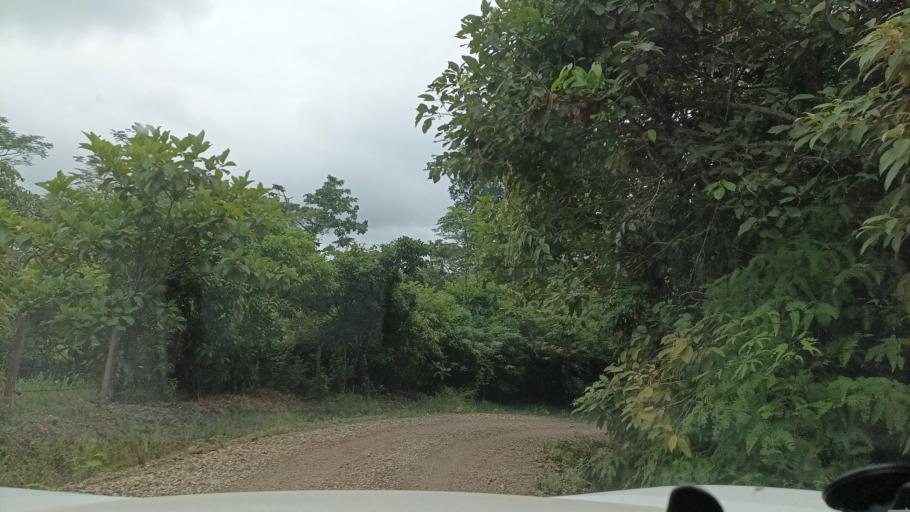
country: MX
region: Veracruz
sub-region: Uxpanapa
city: Poblado 10
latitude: 17.4363
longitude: -94.4153
